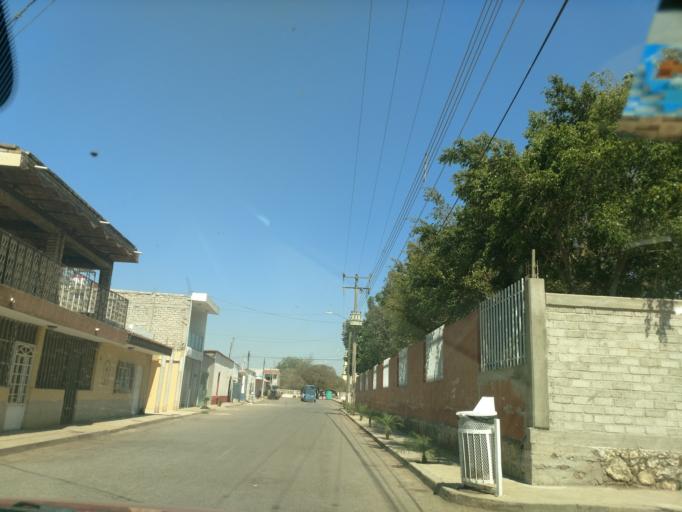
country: MX
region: Nayarit
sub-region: Tepic
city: La Corregidora
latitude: 21.5014
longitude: -104.7046
